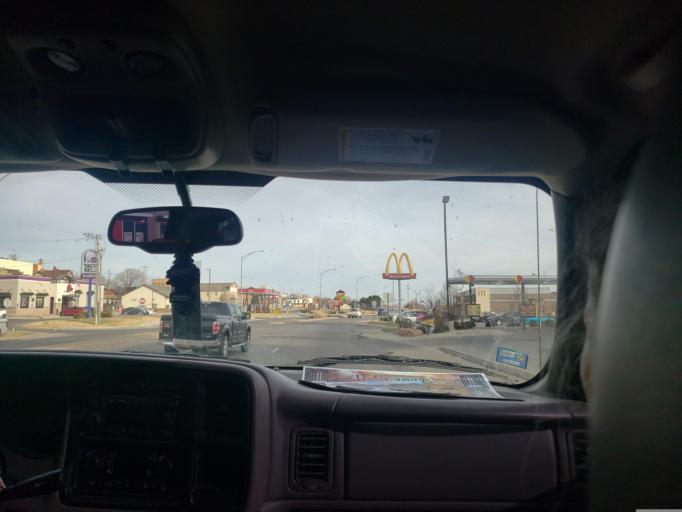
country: US
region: Kansas
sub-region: Ford County
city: Dodge City
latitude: 37.7532
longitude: -100.0249
